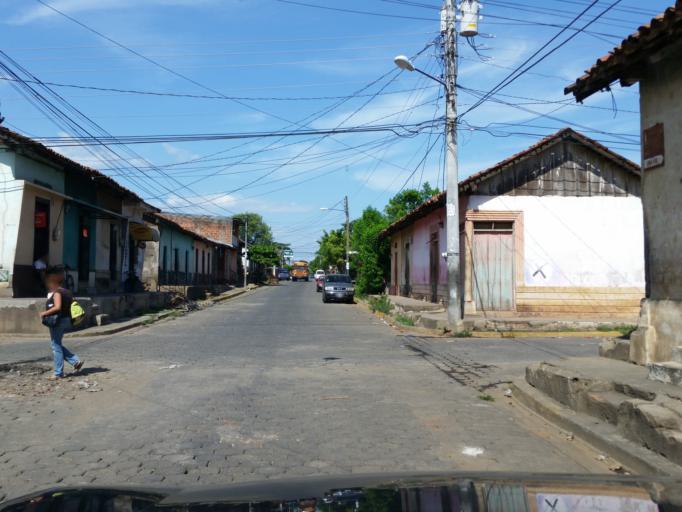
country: NI
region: Leon
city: Leon
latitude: 12.4360
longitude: -86.8935
